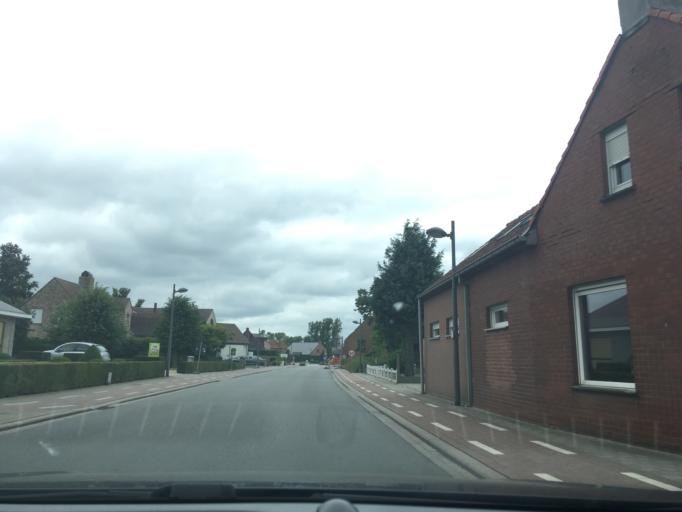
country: BE
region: Flanders
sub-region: Provincie West-Vlaanderen
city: Wingene
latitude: 51.0573
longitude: 3.2841
